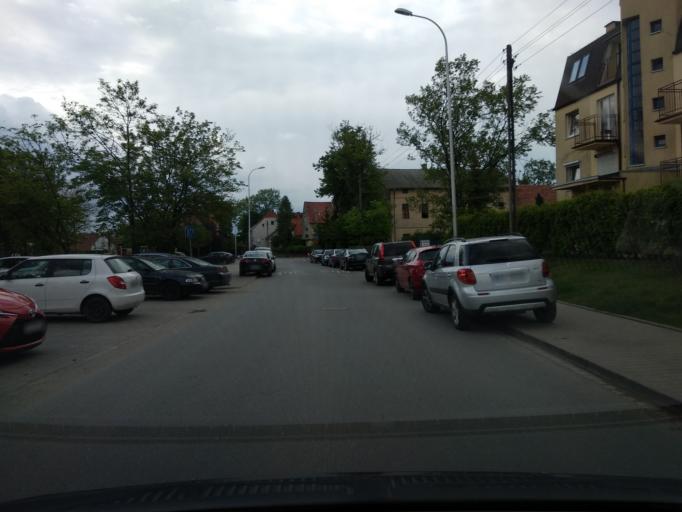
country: PL
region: Lower Silesian Voivodeship
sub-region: Powiat wroclawski
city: Wroclaw
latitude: 51.0642
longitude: 17.0381
